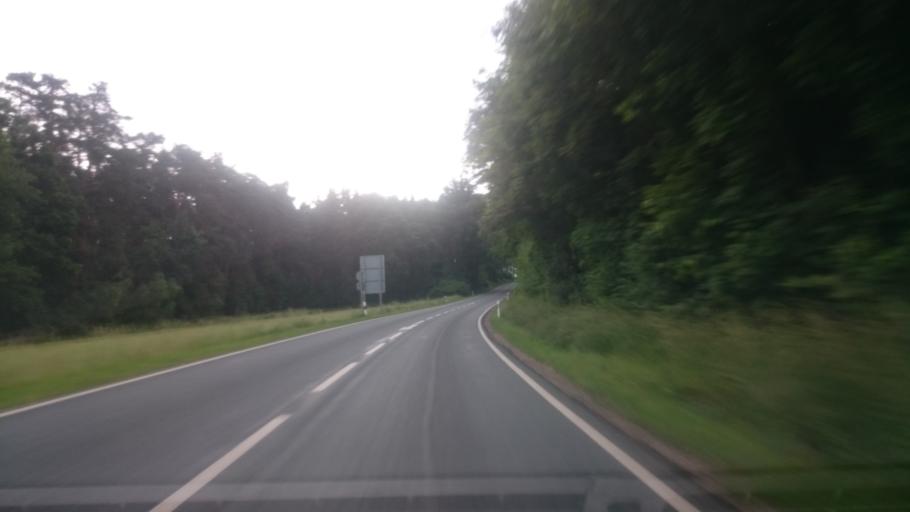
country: DE
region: Bavaria
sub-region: Regierungsbezirk Mittelfranken
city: Hilpoltstein
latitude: 49.1712
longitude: 11.1790
